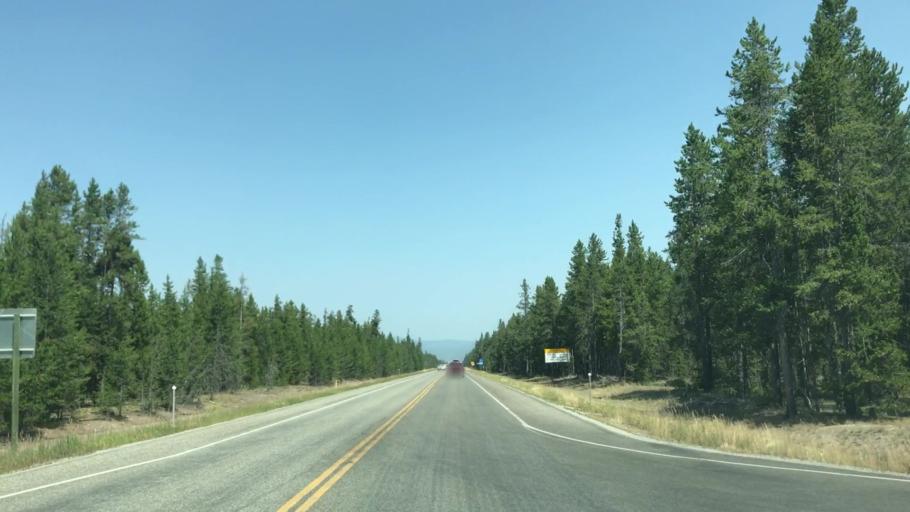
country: US
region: Montana
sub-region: Gallatin County
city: West Yellowstone
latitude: 44.6748
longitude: -111.1004
